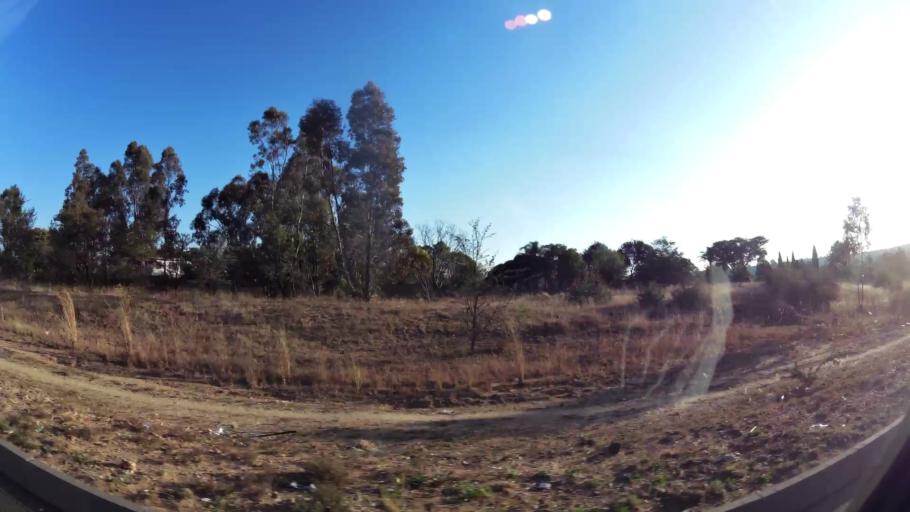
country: ZA
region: Gauteng
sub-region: City of Johannesburg Metropolitan Municipality
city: Midrand
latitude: -25.9996
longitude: 28.1189
